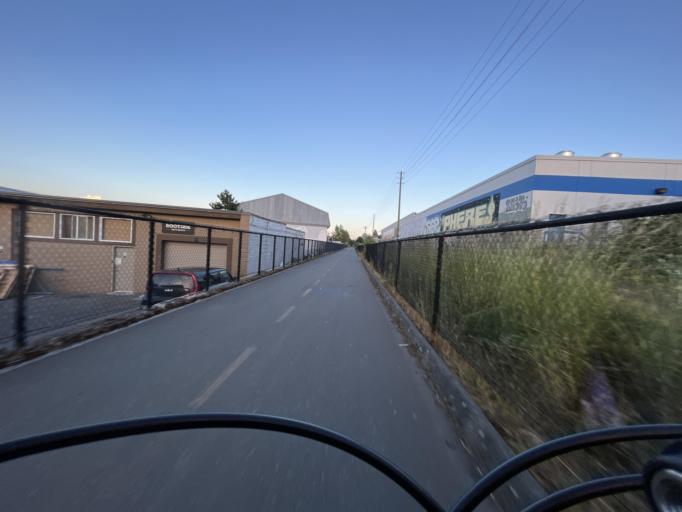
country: CA
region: British Columbia
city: Victoria
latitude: 48.4354
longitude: -123.3976
